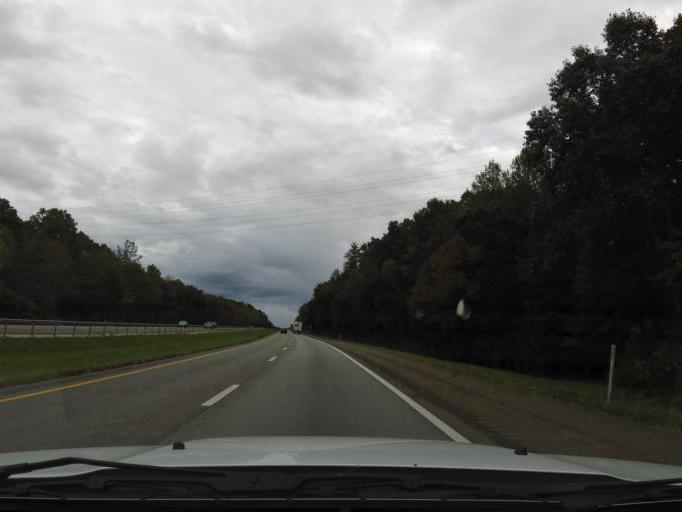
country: US
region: Kentucky
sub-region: Whitley County
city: Corbin
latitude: 36.8705
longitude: -84.1474
